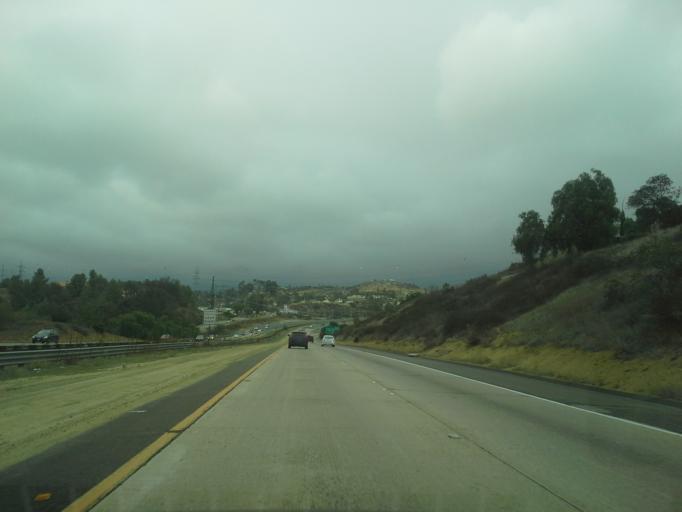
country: US
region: California
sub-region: San Diego County
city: Crest
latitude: 32.8395
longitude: -116.8883
